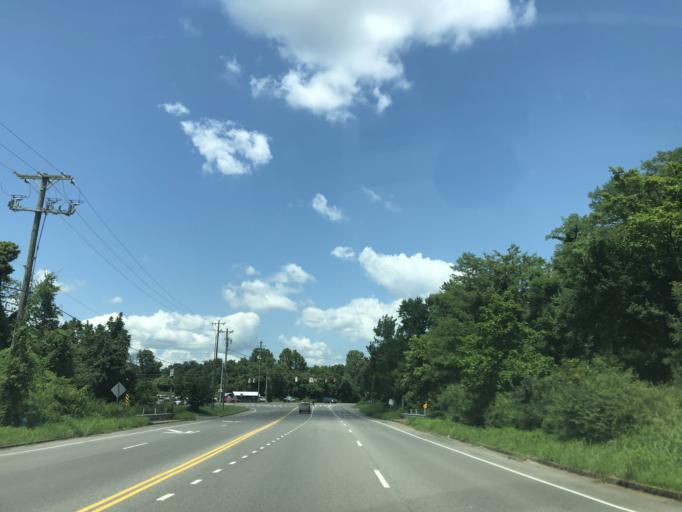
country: US
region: Tennessee
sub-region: Wilson County
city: Green Hill
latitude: 36.2138
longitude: -86.5888
